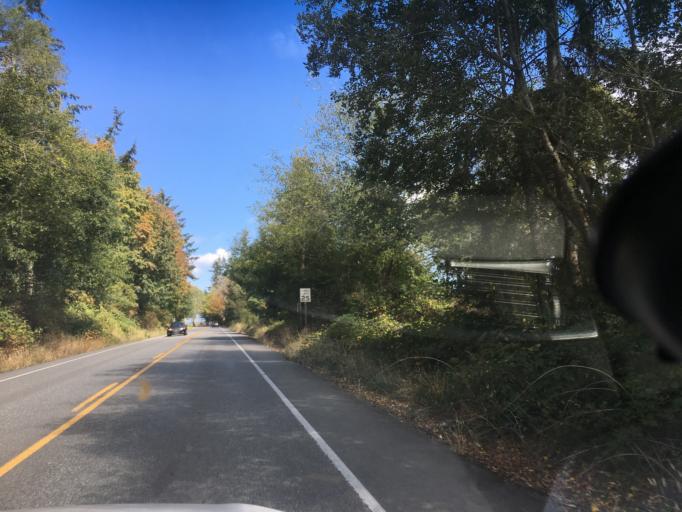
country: US
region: Washington
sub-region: Kitsap County
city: Hansville
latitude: 47.8487
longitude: -122.5848
